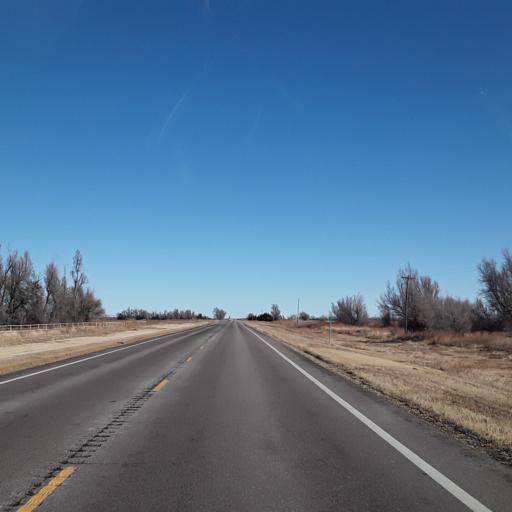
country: US
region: Kansas
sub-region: Pawnee County
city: Larned
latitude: 38.1184
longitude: -99.1814
